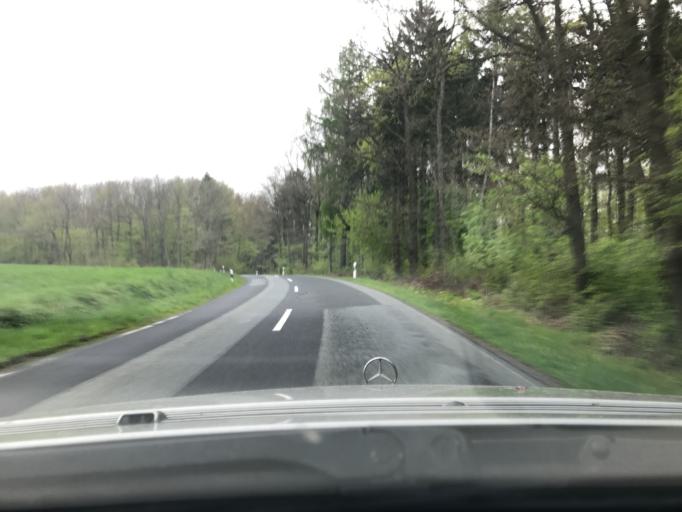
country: DE
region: Thuringia
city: Kefferhausen
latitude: 51.3241
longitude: 10.2742
